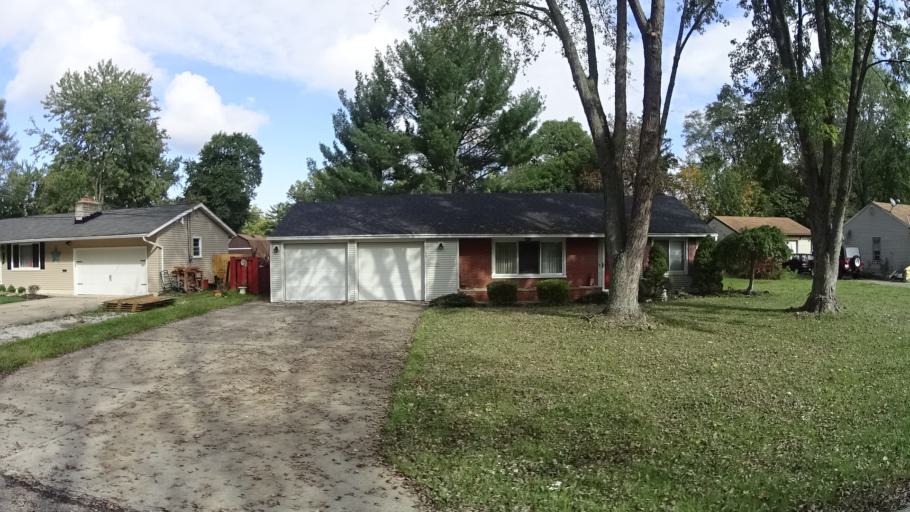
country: US
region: Ohio
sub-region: Lorain County
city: Grafton
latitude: 41.3149
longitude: -82.0741
